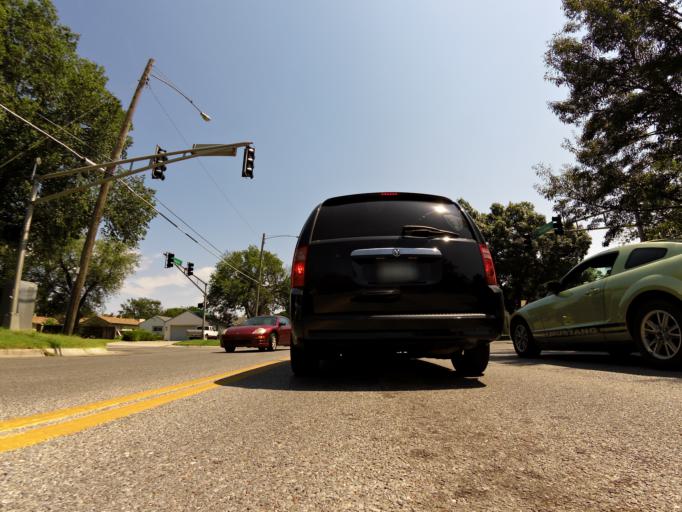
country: US
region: Kansas
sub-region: Sedgwick County
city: Wichita
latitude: 37.6865
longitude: -97.2716
